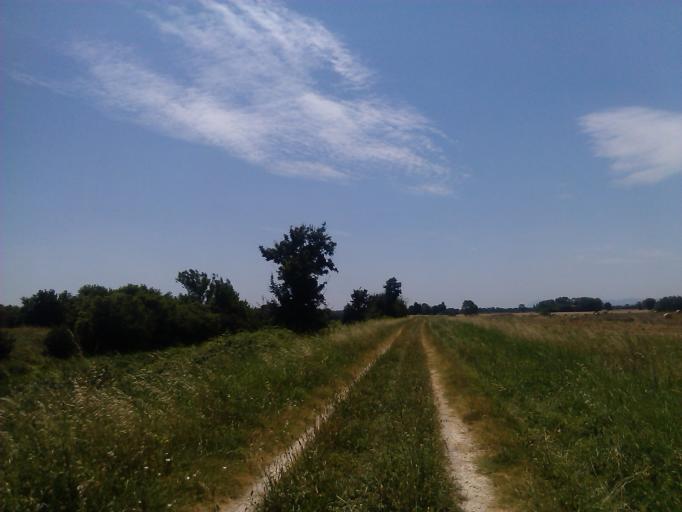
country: IT
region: Tuscany
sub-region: Province of Arezzo
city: Cesa
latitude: 43.3279
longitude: 11.8322
